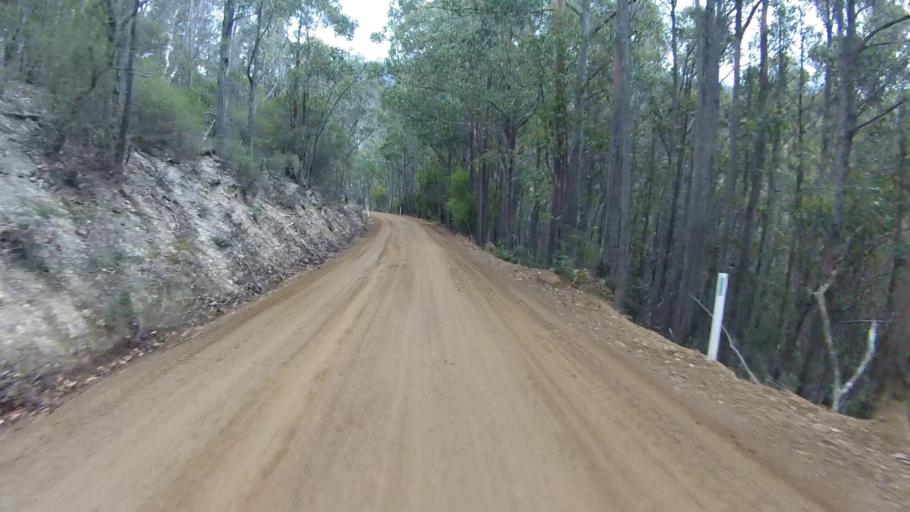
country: AU
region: Tasmania
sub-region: Huon Valley
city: Huonville
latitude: -42.9651
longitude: 147.0479
